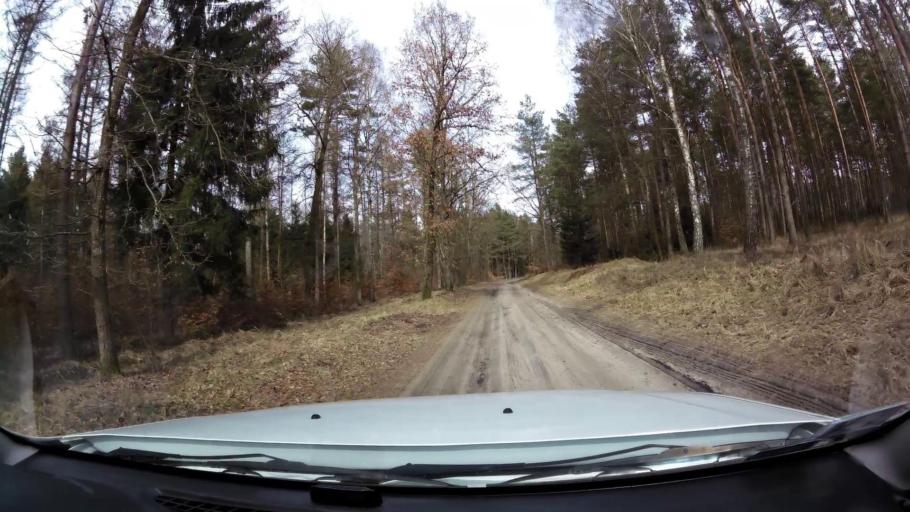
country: PL
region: West Pomeranian Voivodeship
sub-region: Powiat drawski
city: Drawsko Pomorskie
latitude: 53.4914
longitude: 15.7012
